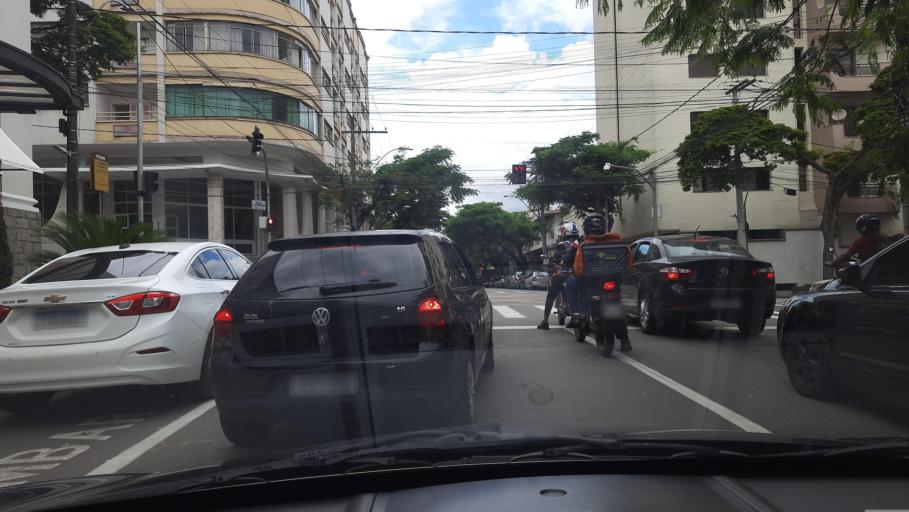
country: BR
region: Minas Gerais
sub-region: Pocos De Caldas
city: Pocos de Caldas
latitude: -21.7844
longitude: -46.5676
